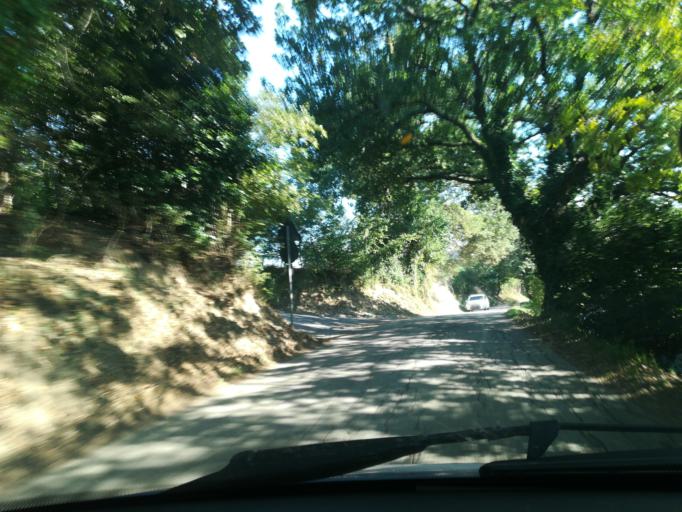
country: IT
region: The Marches
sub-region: Provincia di Macerata
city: Piediripa
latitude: 43.2990
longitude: 13.4805
